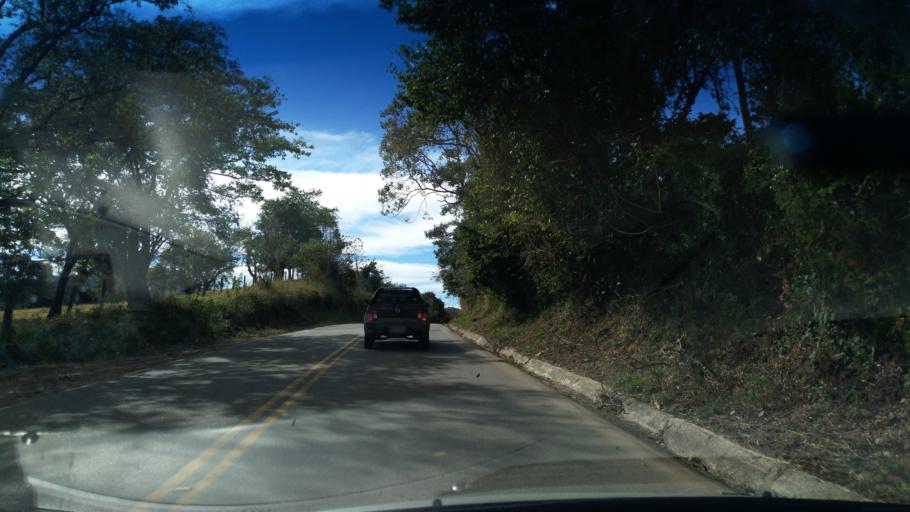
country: BR
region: Minas Gerais
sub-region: Andradas
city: Andradas
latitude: -22.0683
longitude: -46.4531
